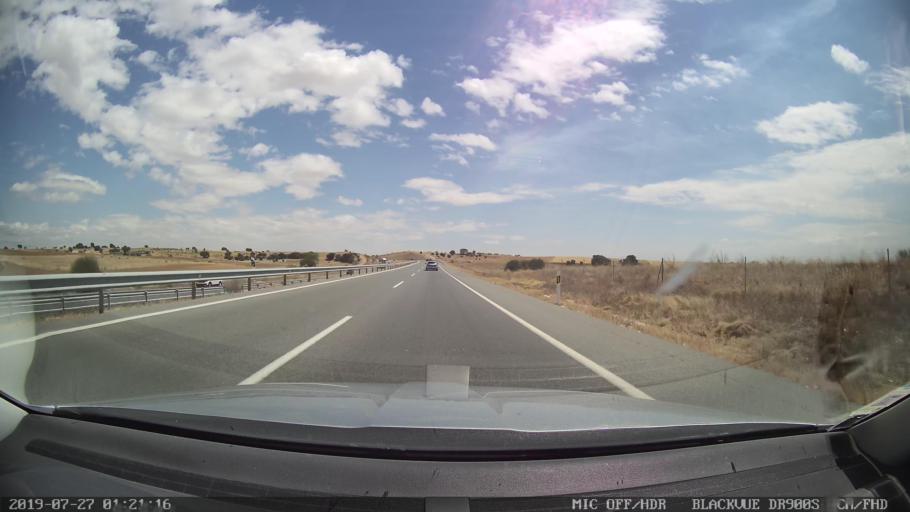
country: ES
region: Castille-La Mancha
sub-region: Province of Toledo
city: Quismondo
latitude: 40.1182
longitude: -4.2838
